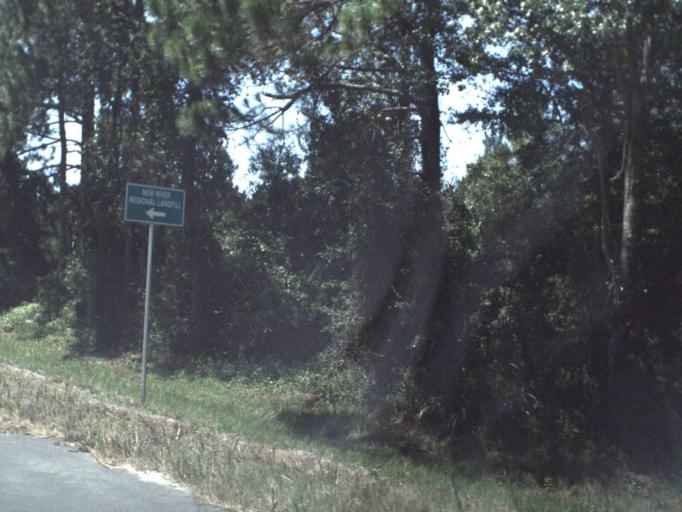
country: US
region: Florida
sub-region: Union County
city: Lake Butler
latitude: 30.1022
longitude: -82.2167
